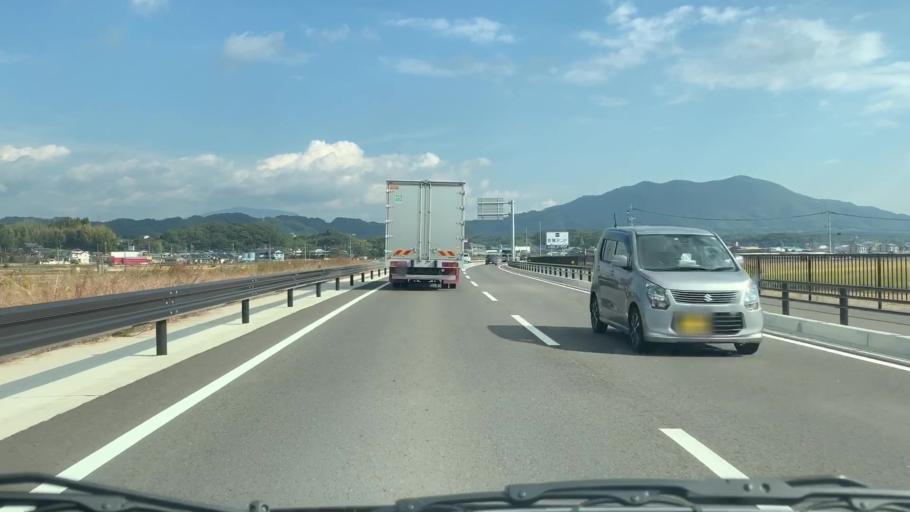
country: JP
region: Saga Prefecture
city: Takeocho-takeo
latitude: 33.2158
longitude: 130.0533
